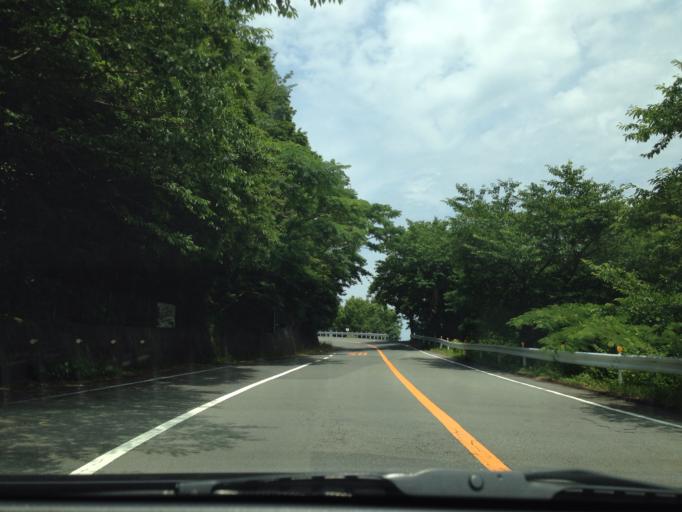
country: JP
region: Shizuoka
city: Heda
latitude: 34.8945
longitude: 138.7680
